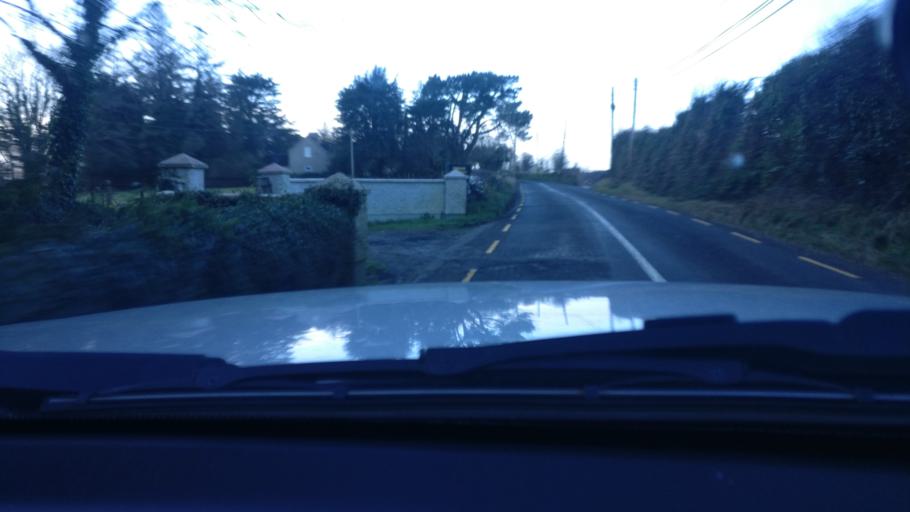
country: IE
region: Connaught
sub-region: County Galway
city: Loughrea
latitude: 53.2274
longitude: -8.4146
